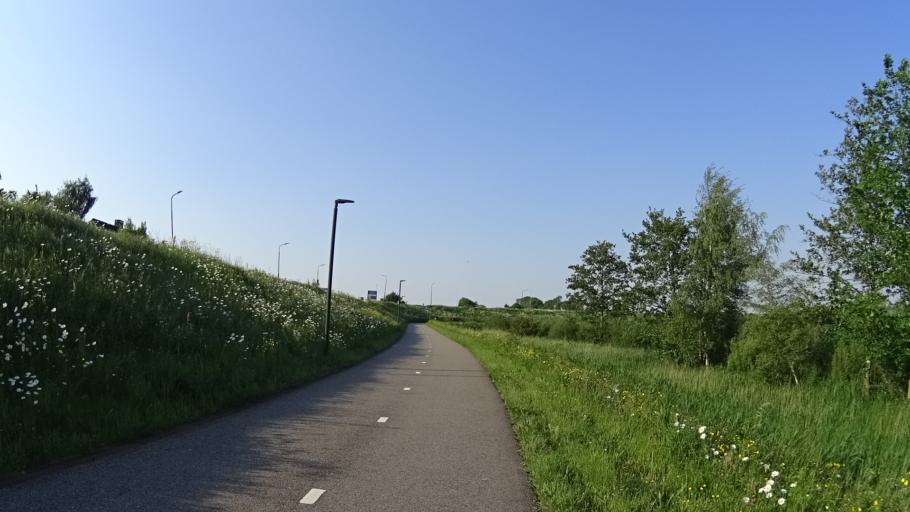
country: NL
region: South Holland
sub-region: Gemeente Giessenlanden
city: Giessenburg
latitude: 51.8366
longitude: 4.9138
